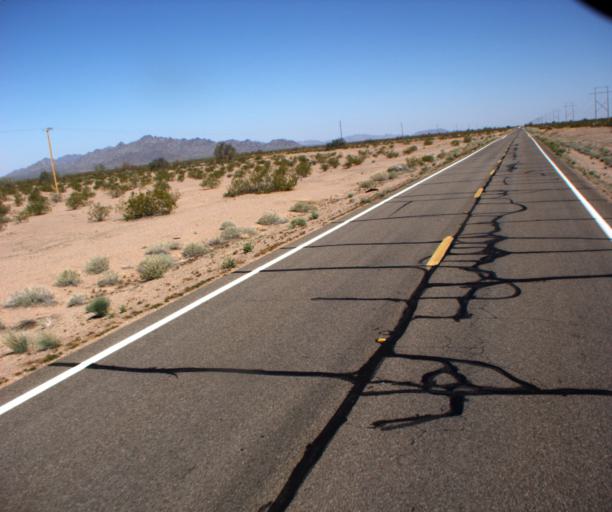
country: US
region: Arizona
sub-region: La Paz County
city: Quartzsite
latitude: 33.4241
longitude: -114.2170
